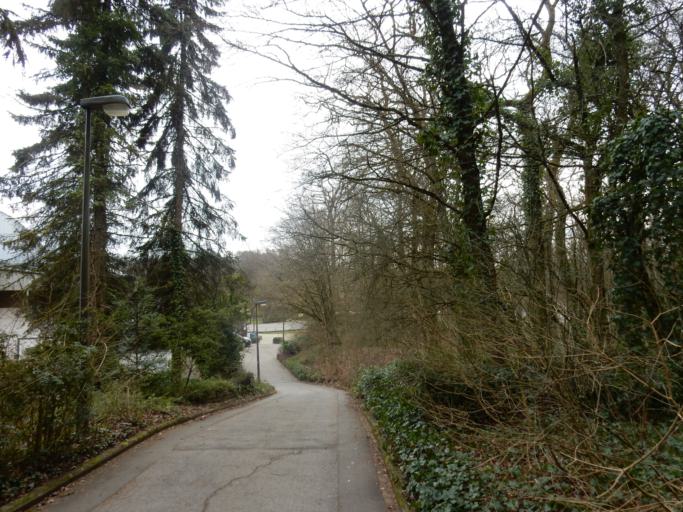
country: LU
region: Luxembourg
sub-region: Canton d'Esch-sur-Alzette
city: Leudelange
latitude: 49.5687
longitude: 6.1081
